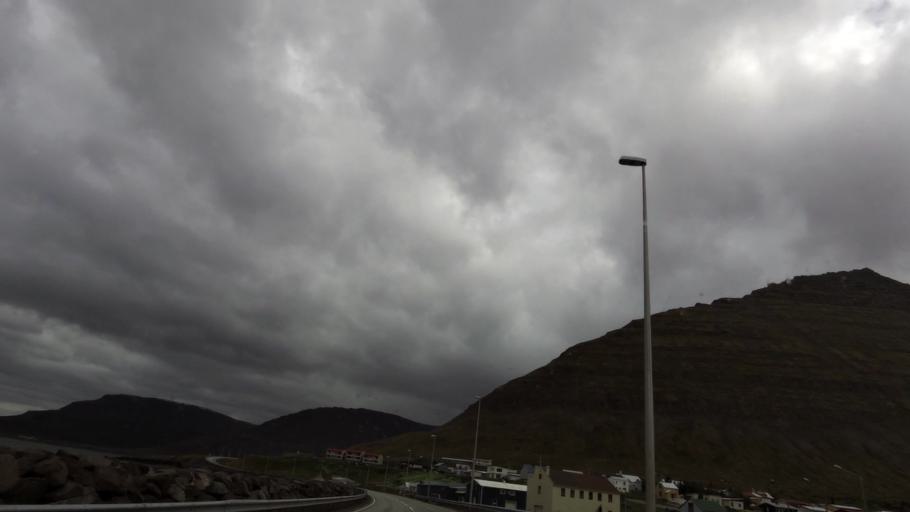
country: IS
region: Westfjords
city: Isafjoerdur
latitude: 66.1118
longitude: -23.1209
